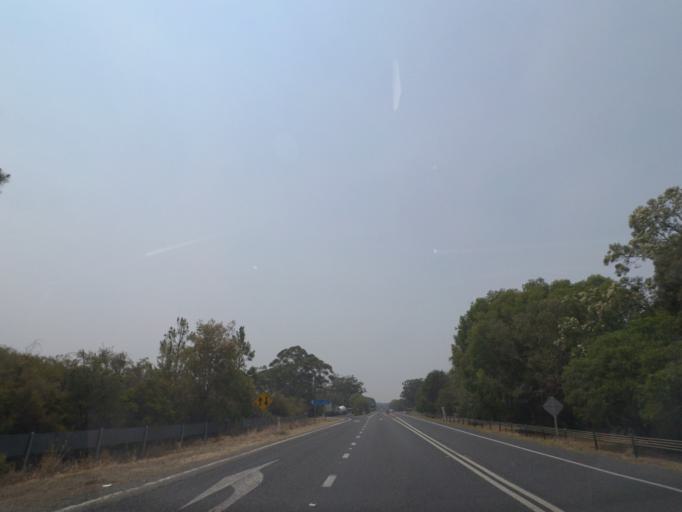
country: AU
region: New South Wales
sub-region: Ballina
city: Ballina
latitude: -28.9359
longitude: 153.4714
